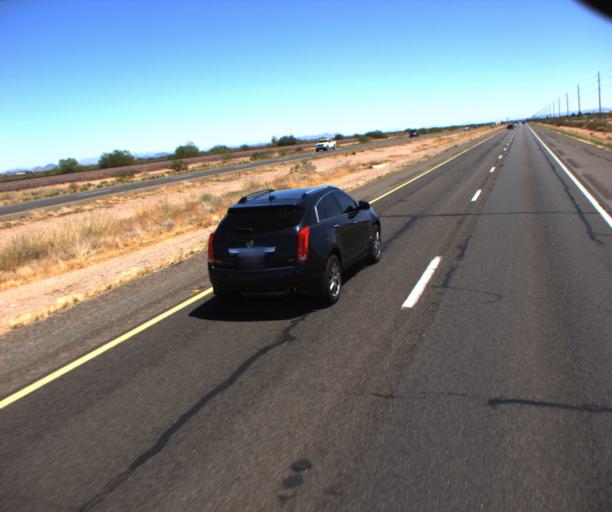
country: US
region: Arizona
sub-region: Maricopa County
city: Sun City West
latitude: 33.7211
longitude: -112.4561
